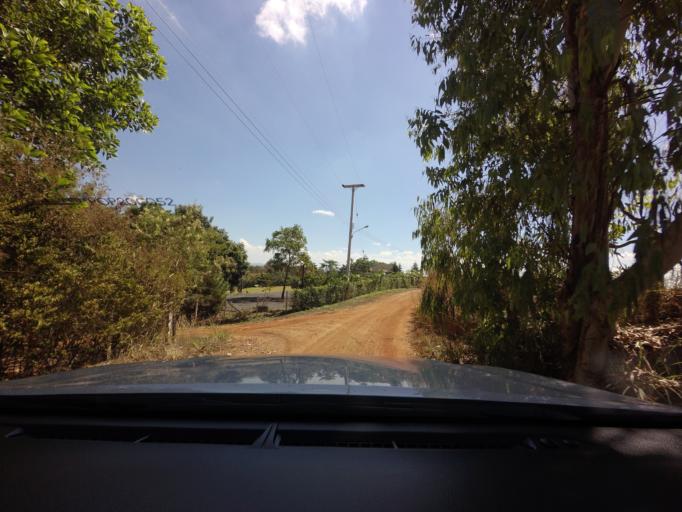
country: TH
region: Nakhon Ratchasima
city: Wang Nam Khiao
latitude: 14.4766
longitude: 101.6557
